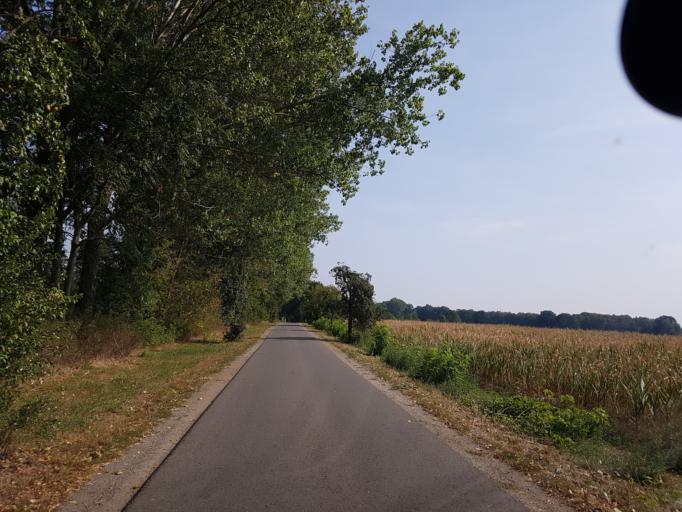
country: DE
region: Brandenburg
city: Finsterwalde
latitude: 51.6871
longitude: 13.7126
